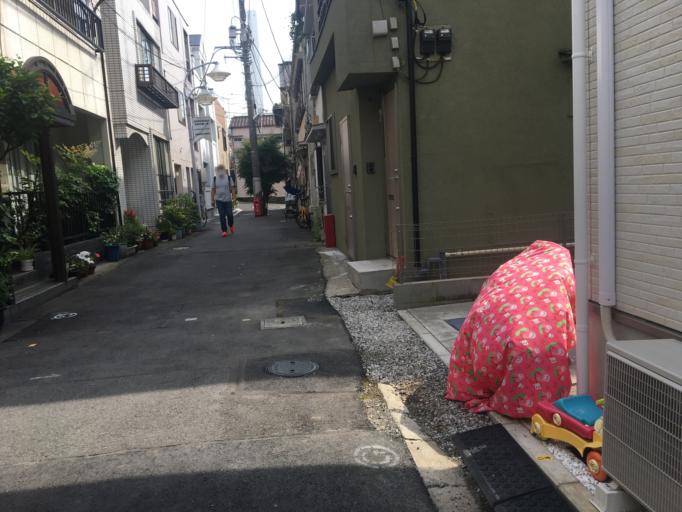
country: JP
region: Tokyo
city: Tokyo
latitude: 35.7407
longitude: 139.7164
